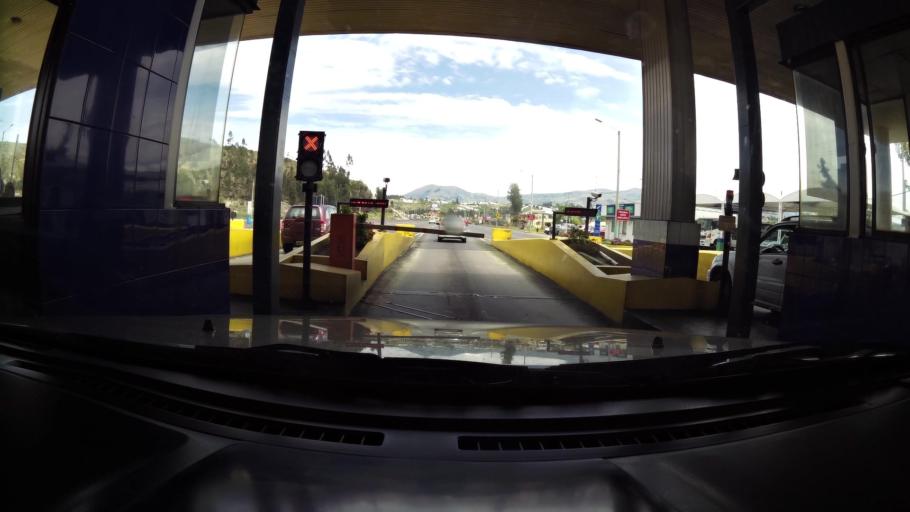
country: EC
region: Cotopaxi
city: San Miguel de Salcedo
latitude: -1.0591
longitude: -78.6018
